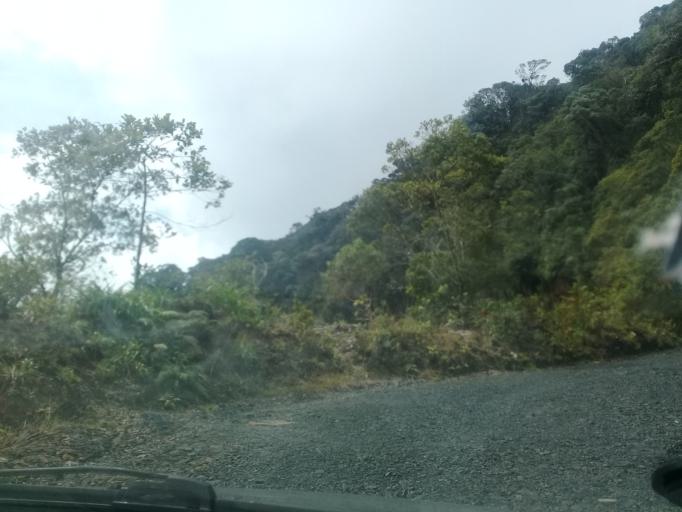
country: CO
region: Cundinamarca
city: Gachala
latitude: 4.7028
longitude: -73.4192
